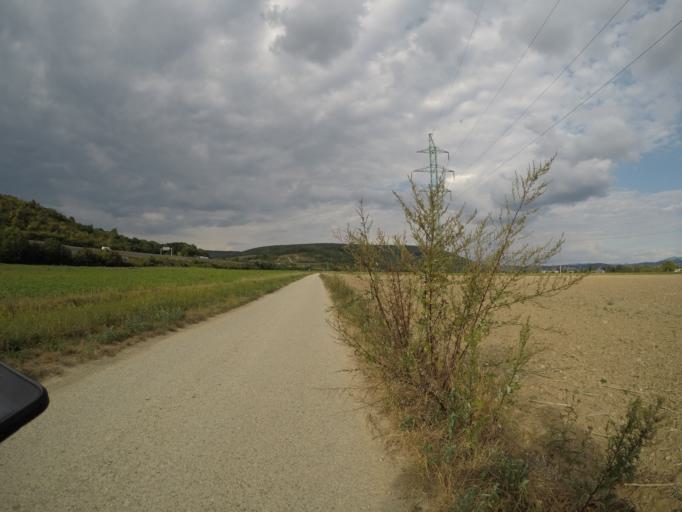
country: SK
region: Trenciansky
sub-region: Okres Trencin
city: Trencin
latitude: 48.9051
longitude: 17.9962
